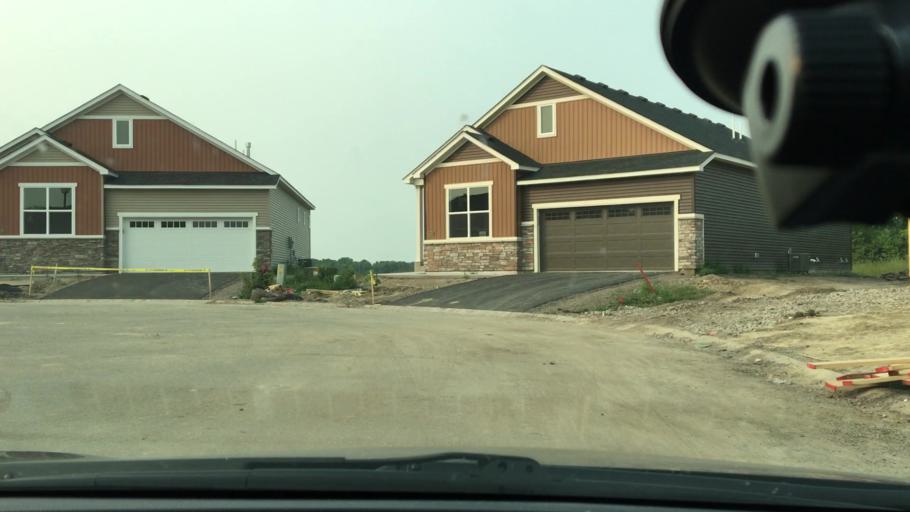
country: US
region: Minnesota
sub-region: Wright County
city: Albertville
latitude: 45.2860
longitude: -93.6770
